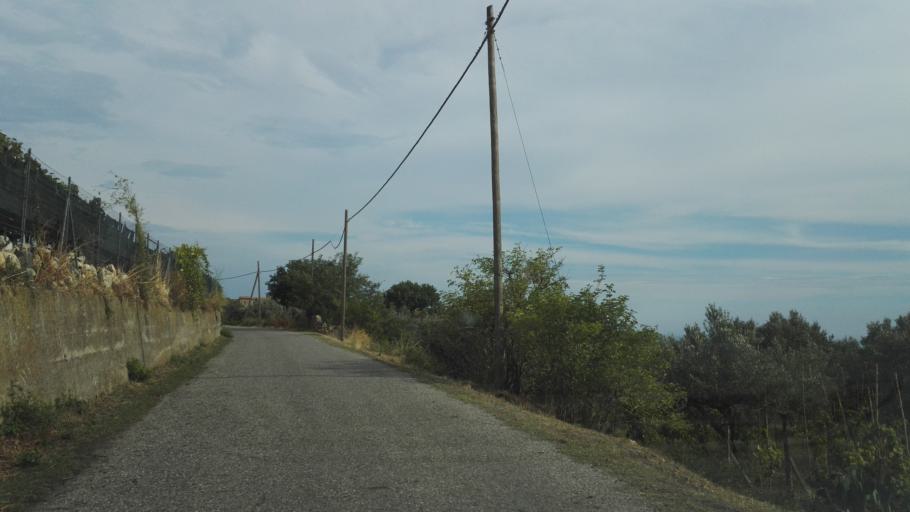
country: IT
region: Calabria
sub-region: Provincia di Reggio Calabria
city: Stignano
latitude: 38.4272
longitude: 16.4627
